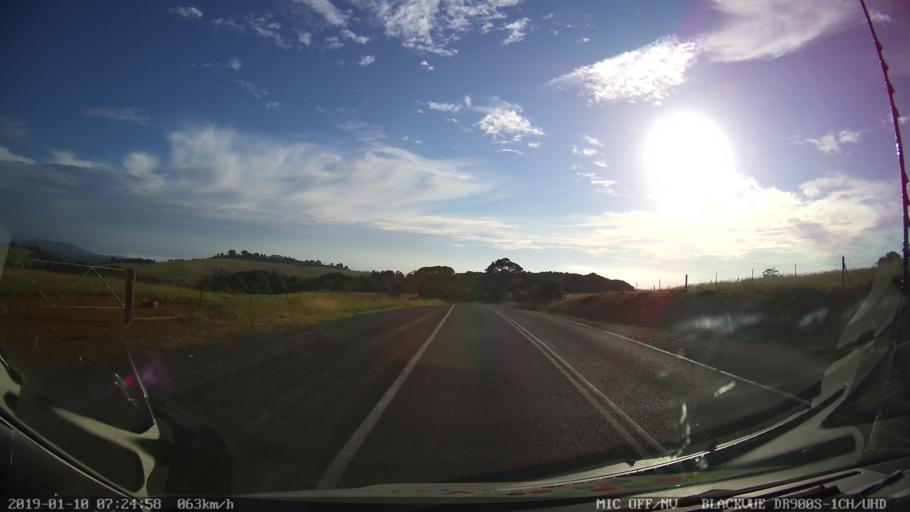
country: AU
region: New South Wales
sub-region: Bellingen
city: Dorrigo
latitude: -30.3714
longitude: 152.5844
